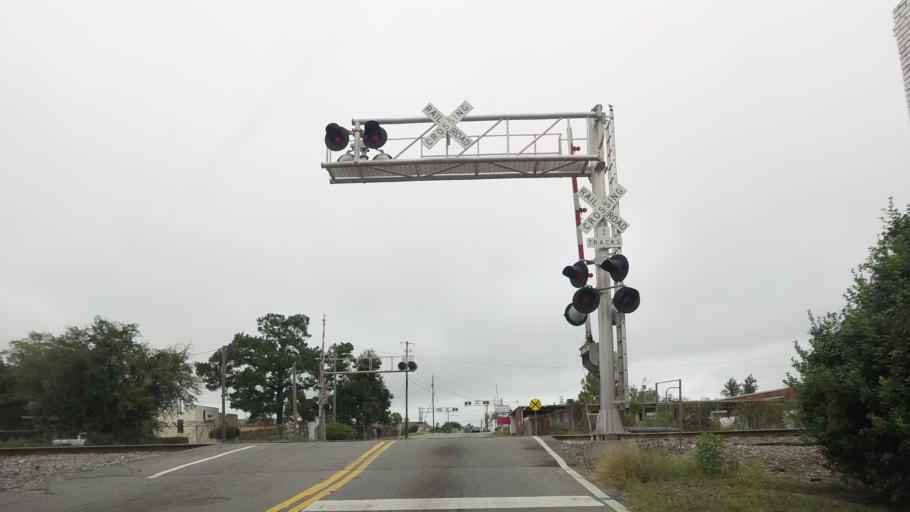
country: US
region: Georgia
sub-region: Lowndes County
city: Valdosta
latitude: 30.8267
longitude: -83.2801
